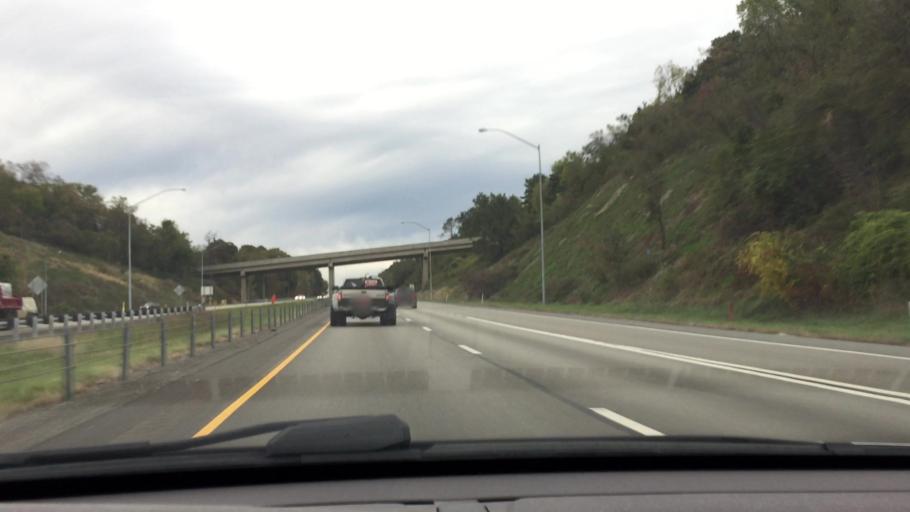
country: US
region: Pennsylvania
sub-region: Beaver County
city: Ambridge
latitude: 40.5599
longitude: -80.2796
